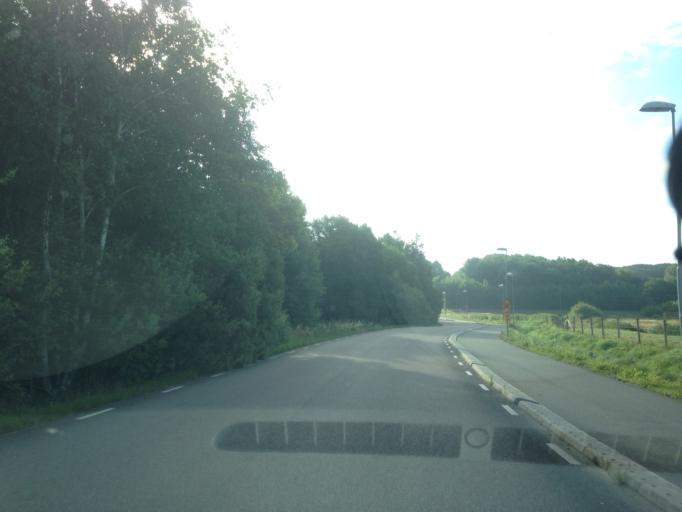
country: SE
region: Vaestra Goetaland
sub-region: Goteborg
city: Goeteborg
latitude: 57.7684
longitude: 11.9395
